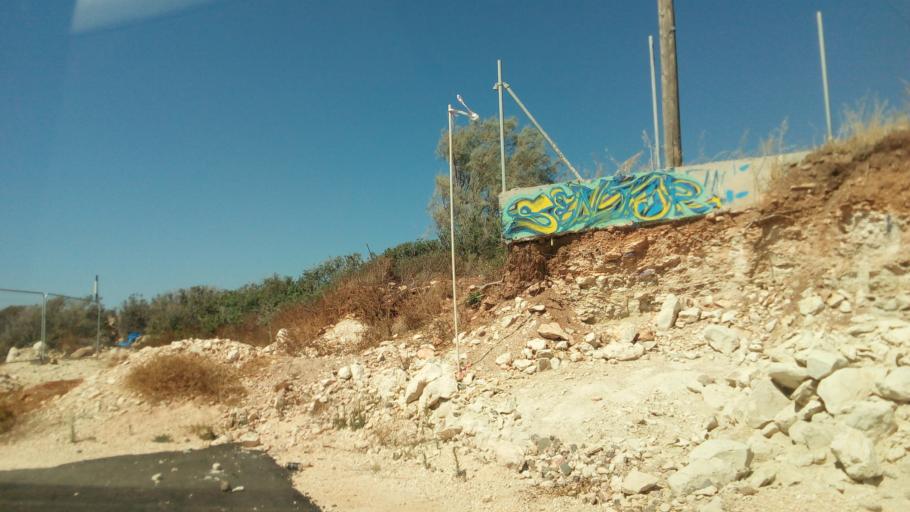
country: CY
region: Pafos
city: Pegeia
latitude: 34.8961
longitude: 32.3265
